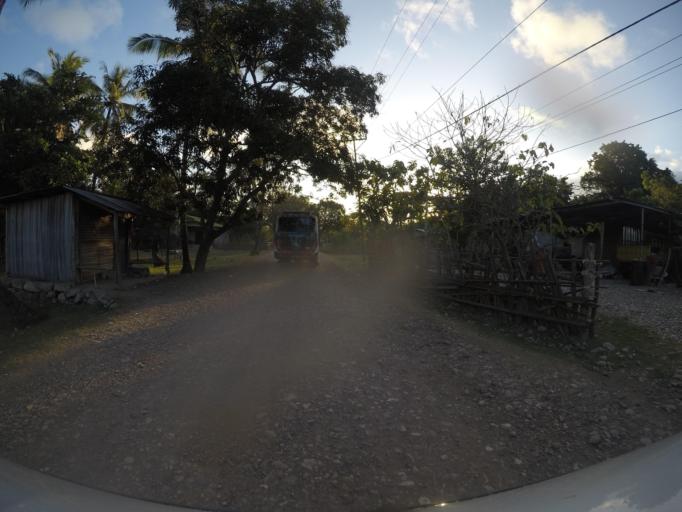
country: TL
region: Baucau
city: Venilale
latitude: -8.7481
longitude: 126.7072
